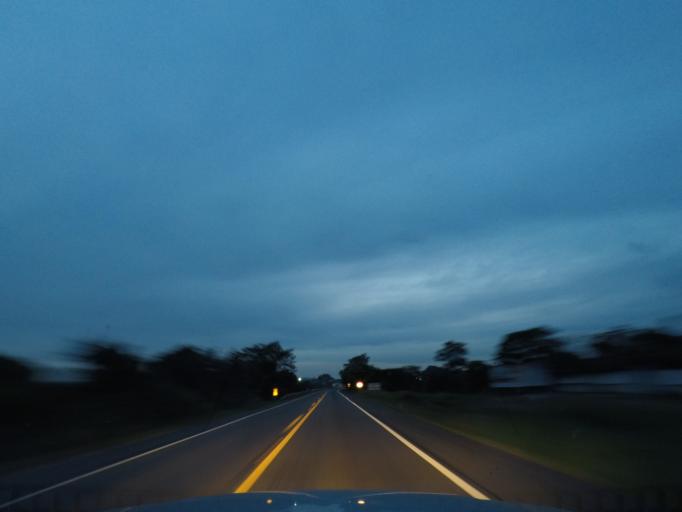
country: BR
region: Bahia
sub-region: Andarai
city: Vera Cruz
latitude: -12.5011
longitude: -41.2866
